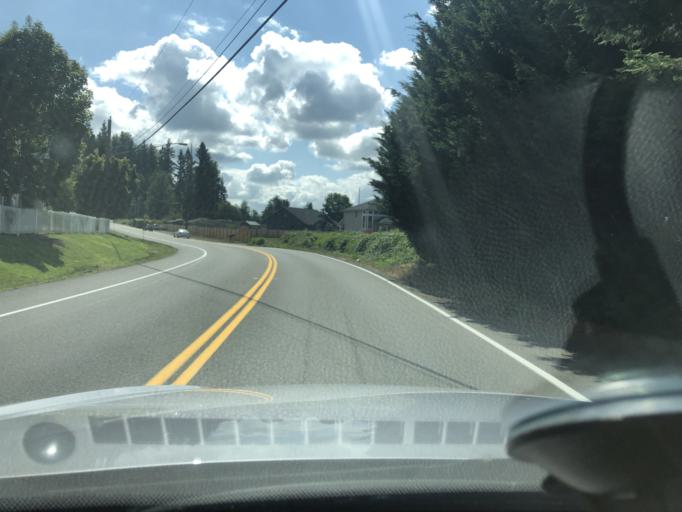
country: US
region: Washington
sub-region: King County
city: Lea Hill
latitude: 47.3178
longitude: -122.2044
